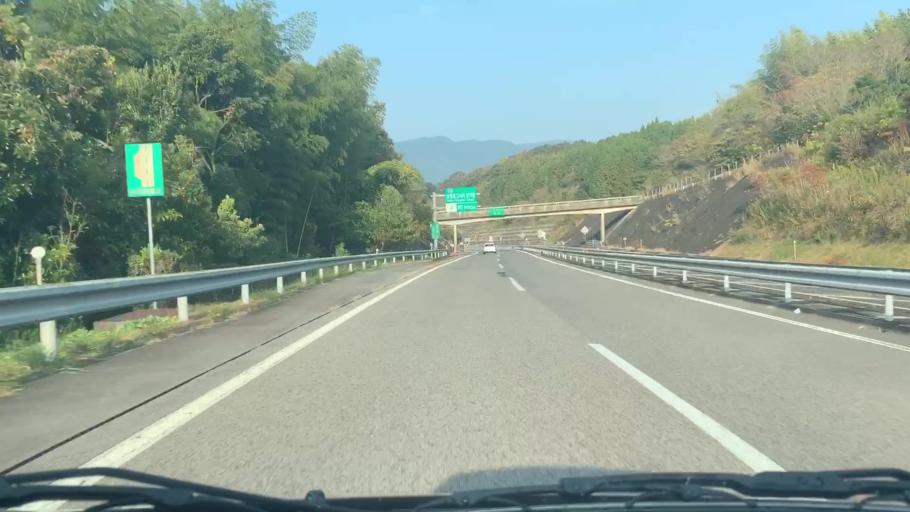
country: JP
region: Saga Prefecture
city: Imaricho-ko
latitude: 33.1671
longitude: 129.8565
